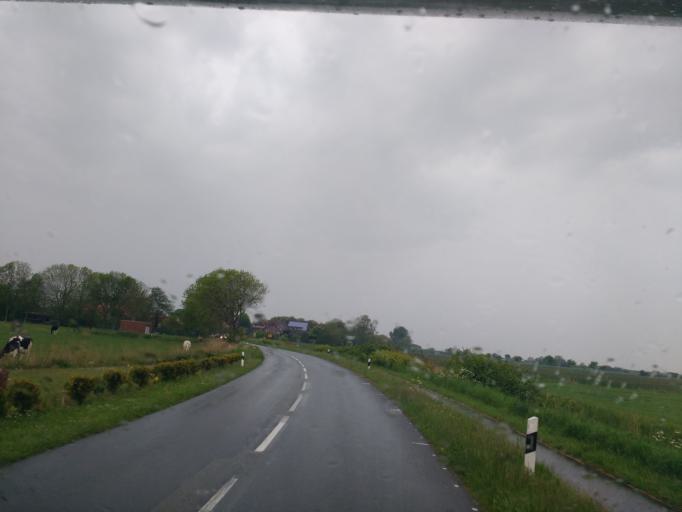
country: DE
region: Lower Saxony
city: Schillig
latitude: 53.7055
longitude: 7.9833
